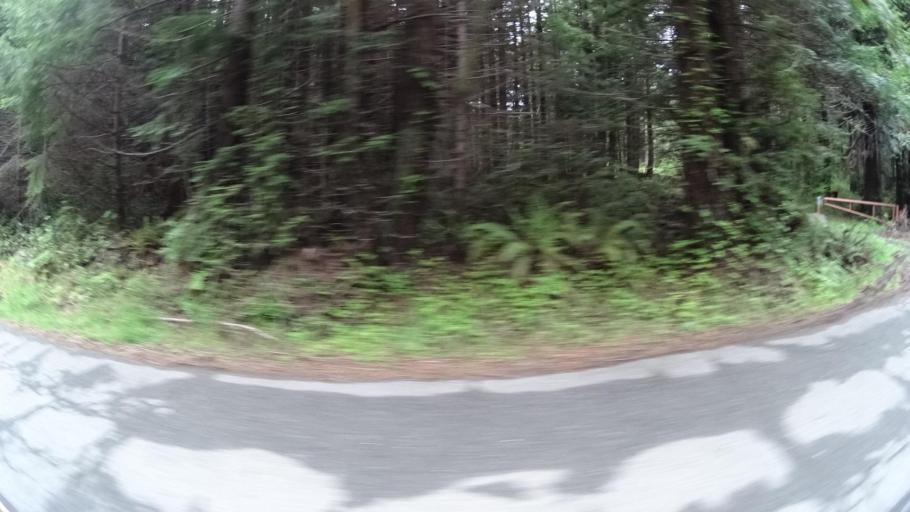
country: US
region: California
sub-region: Humboldt County
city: Blue Lake
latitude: 40.8746
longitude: -123.9691
